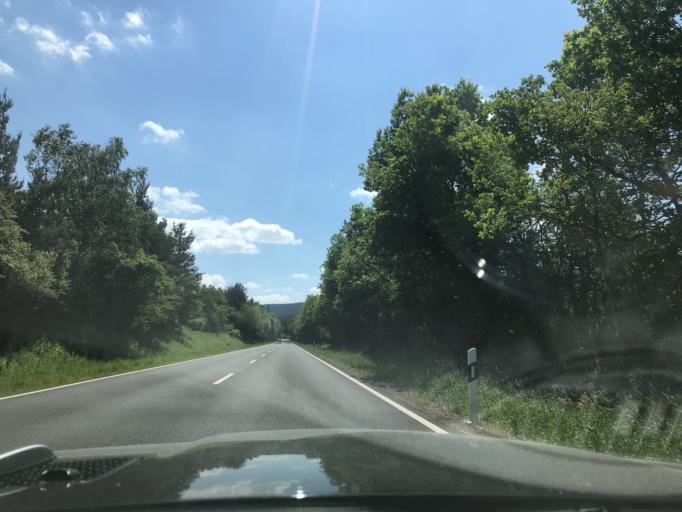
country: DE
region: Thuringia
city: Luisenthal
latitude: 50.8010
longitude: 10.7474
